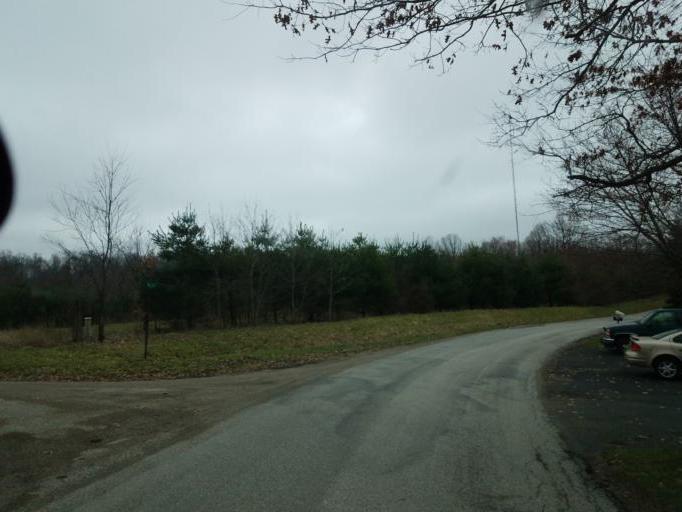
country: US
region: Ohio
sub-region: Sandusky County
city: Bellville
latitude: 40.5875
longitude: -82.4724
